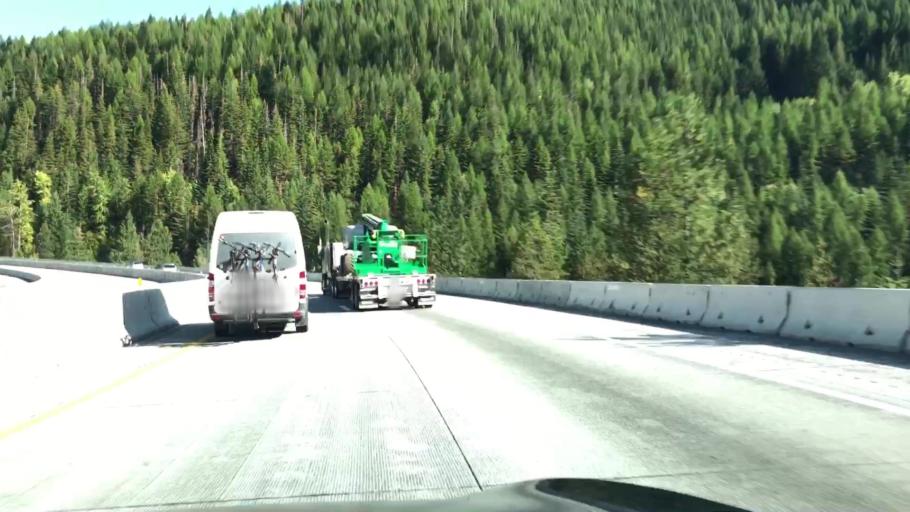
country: US
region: Idaho
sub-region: Shoshone County
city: Wallace
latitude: 47.4597
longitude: -115.7282
